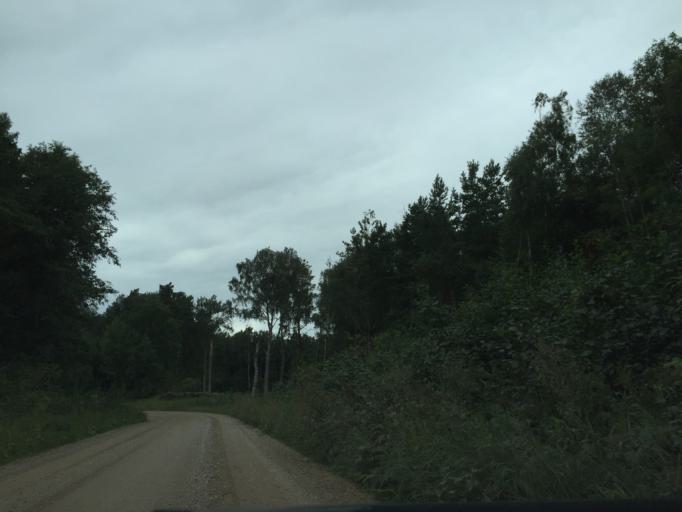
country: LV
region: Jaunpils
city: Jaunpils
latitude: 56.7285
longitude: 23.0751
